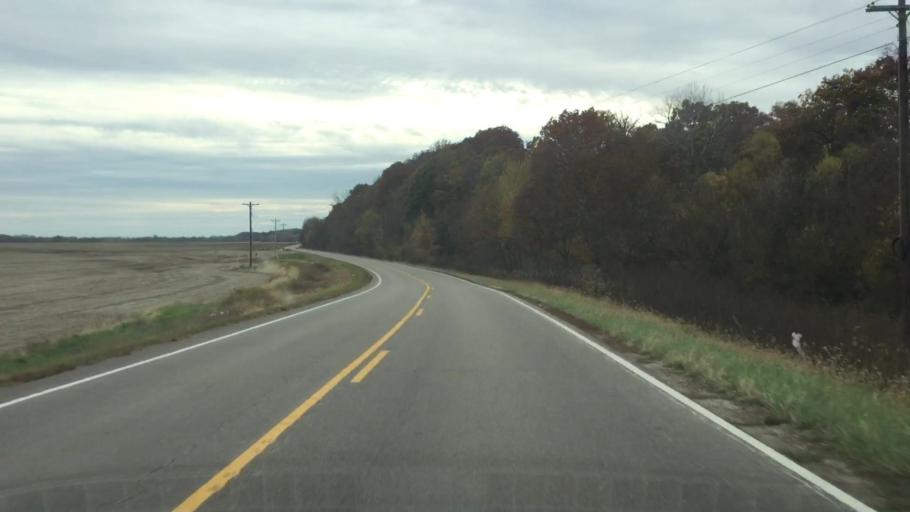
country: US
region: Missouri
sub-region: Callaway County
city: Fulton
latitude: 38.6970
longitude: -91.8292
